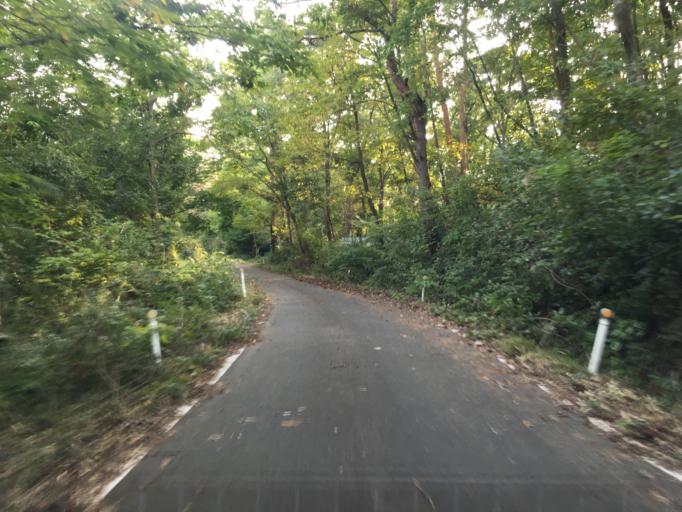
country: JP
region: Fukushima
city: Yanagawamachi-saiwaicho
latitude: 37.8966
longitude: 140.5441
